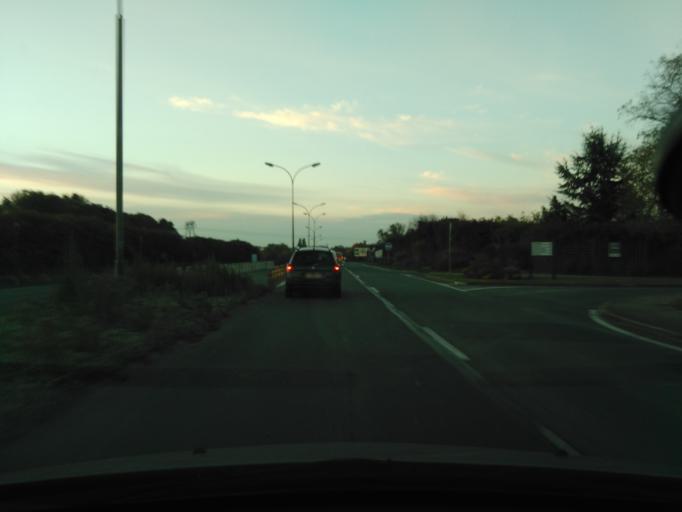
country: FR
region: Poitou-Charentes
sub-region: Departement de la Charente-Maritime
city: Lagord
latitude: 46.1835
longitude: -1.1524
